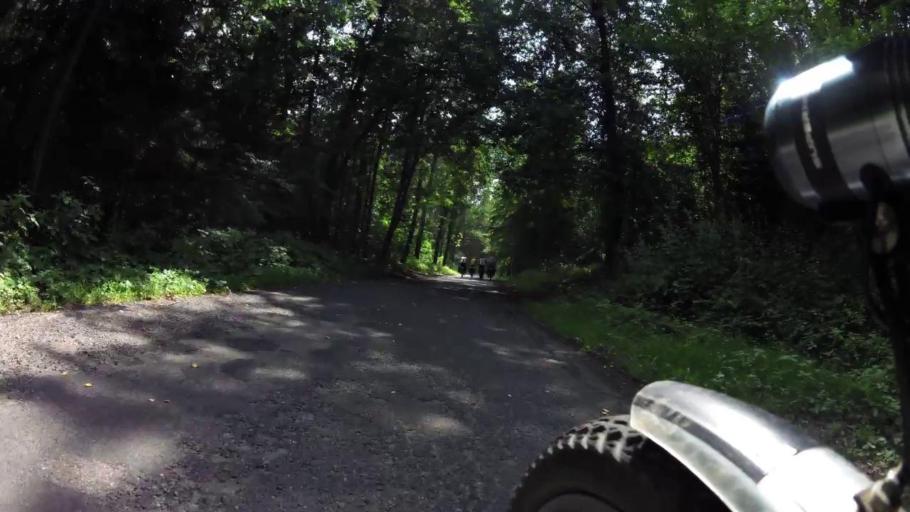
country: PL
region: West Pomeranian Voivodeship
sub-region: Powiat mysliborski
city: Boleszkowice
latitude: 52.6785
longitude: 14.6014
